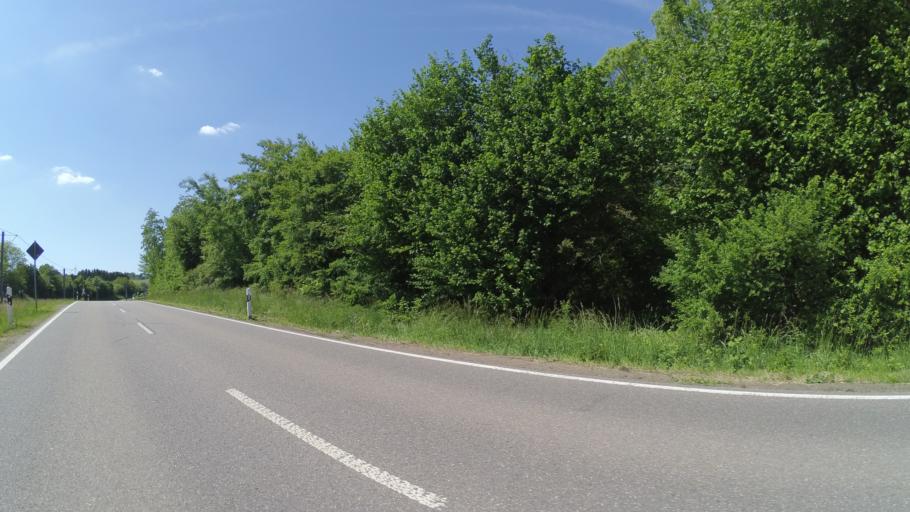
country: DE
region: Saarland
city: Riegelsberg
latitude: 49.3163
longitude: 6.9226
